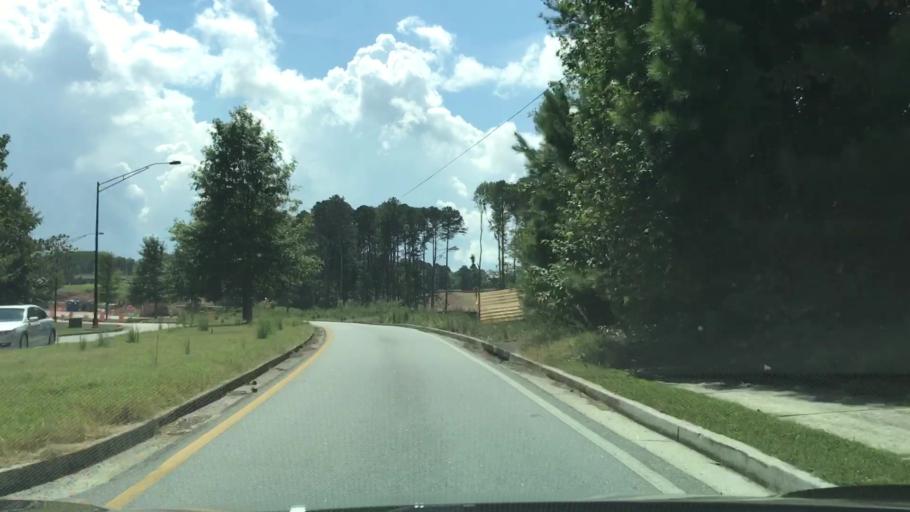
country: US
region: Georgia
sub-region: Gwinnett County
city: Snellville
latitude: 33.8543
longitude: -84.0473
